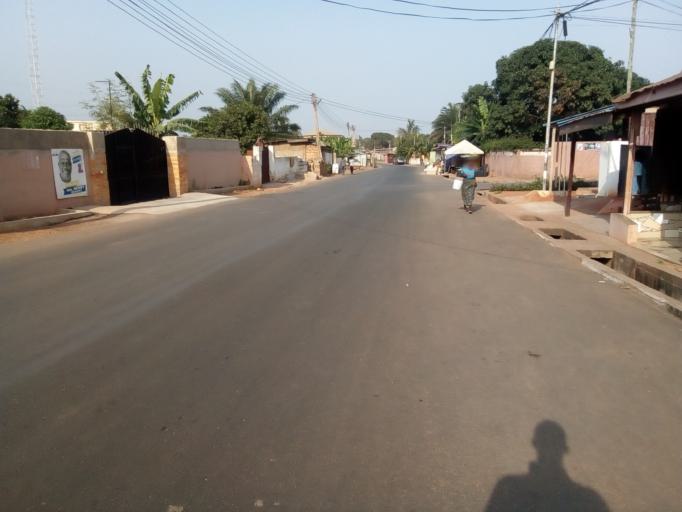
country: GH
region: Greater Accra
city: Accra
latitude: 5.5867
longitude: -0.2153
